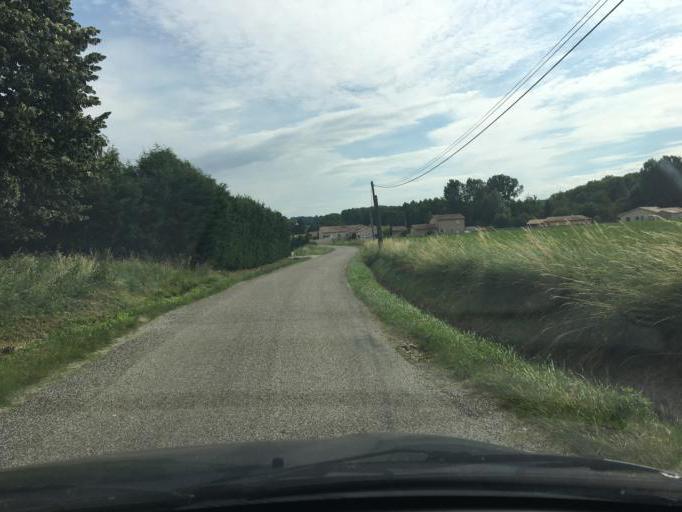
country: FR
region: Rhone-Alpes
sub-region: Departement de la Drome
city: Clerieux
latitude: 45.1102
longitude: 4.9291
